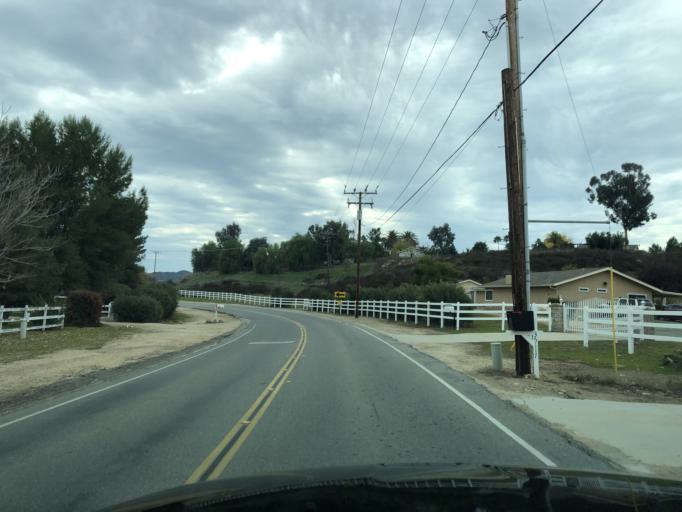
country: US
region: California
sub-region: Riverside County
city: Wildomar
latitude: 33.6112
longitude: -117.2757
